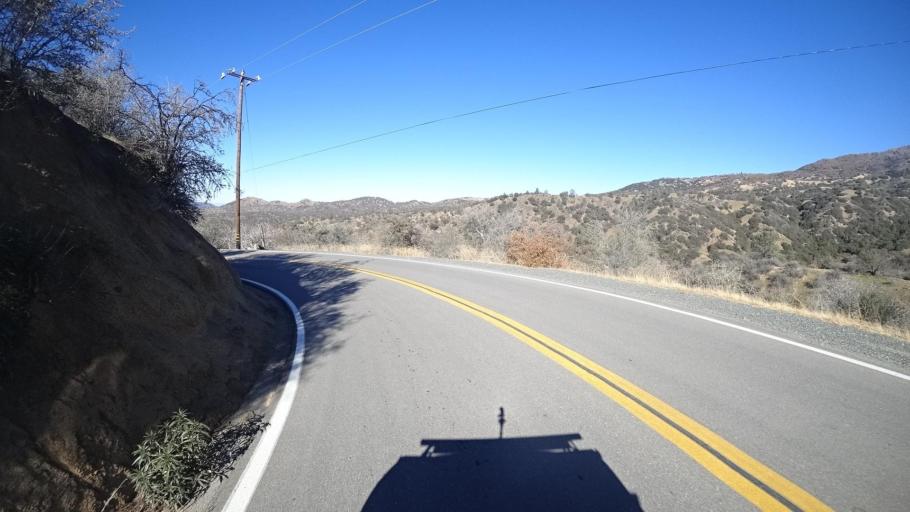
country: US
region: California
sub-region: Kern County
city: Alta Sierra
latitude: 35.7383
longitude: -118.6416
